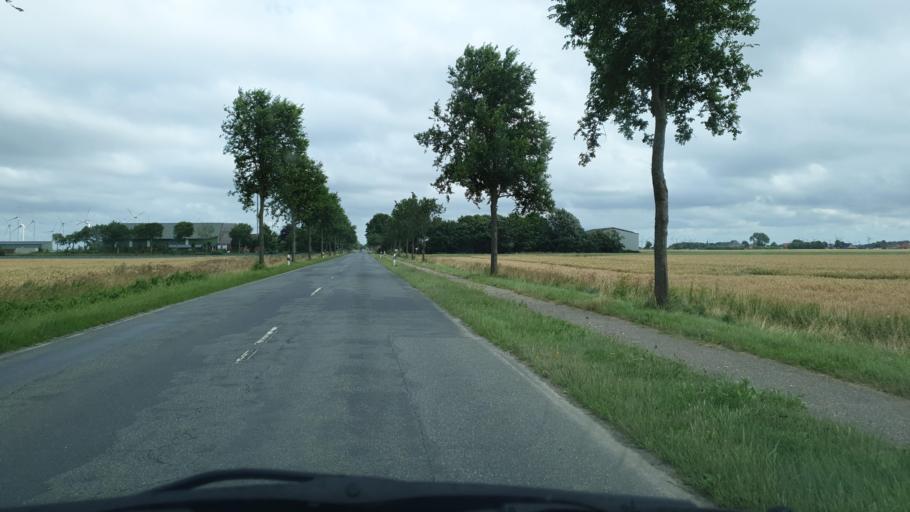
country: DE
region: Schleswig-Holstein
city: Friedrichskoog
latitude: 54.0195
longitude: 8.8829
